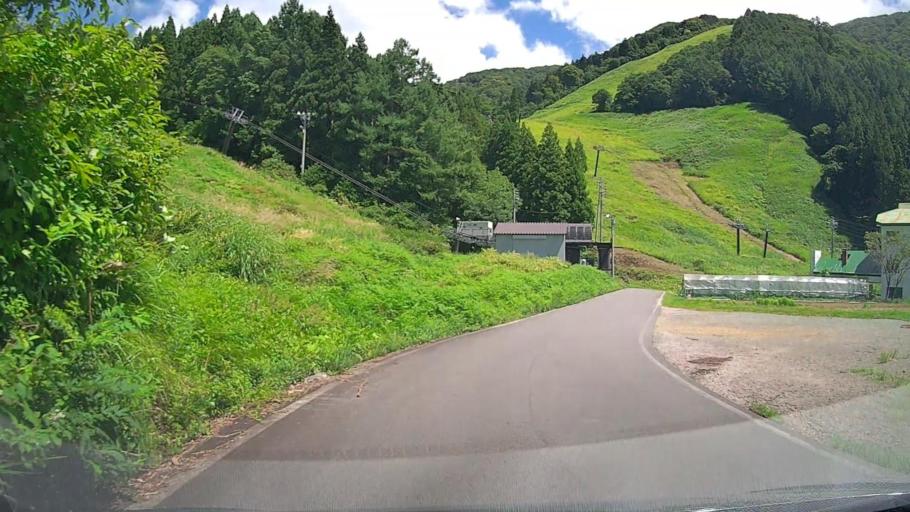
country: JP
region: Nagano
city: Iiyama
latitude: 36.9280
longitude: 138.4551
